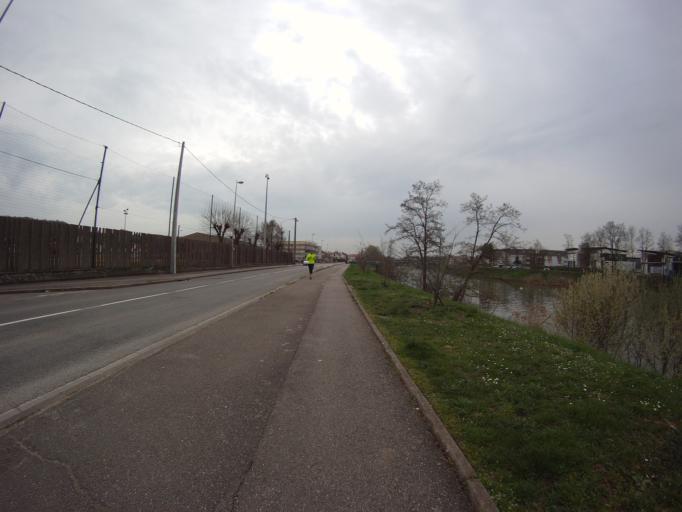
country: FR
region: Lorraine
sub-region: Departement de Meurthe-et-Moselle
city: Malzeville
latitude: 48.7124
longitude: 6.1775
